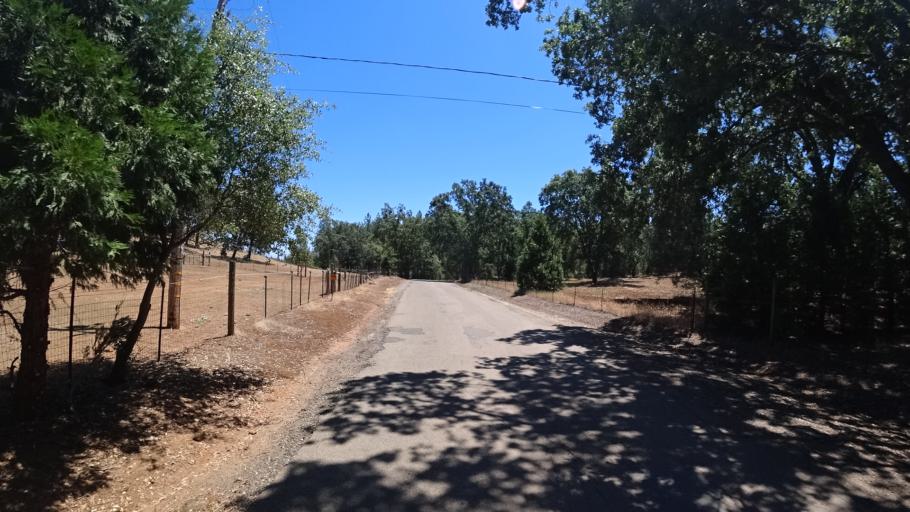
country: US
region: California
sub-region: Calaveras County
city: Mountain Ranch
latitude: 38.2457
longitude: -120.5822
